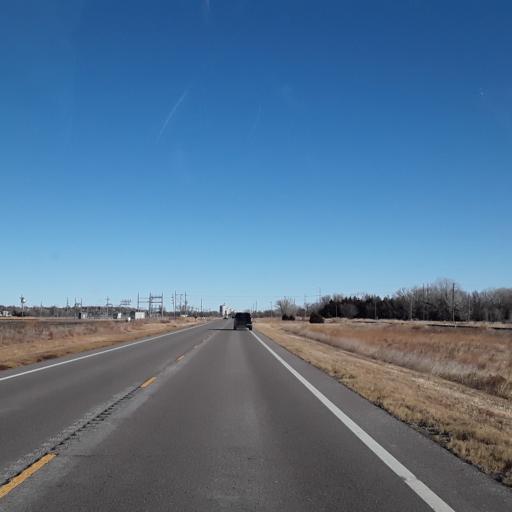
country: US
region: Kansas
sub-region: Pawnee County
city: Larned
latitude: 38.1574
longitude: -99.1252
